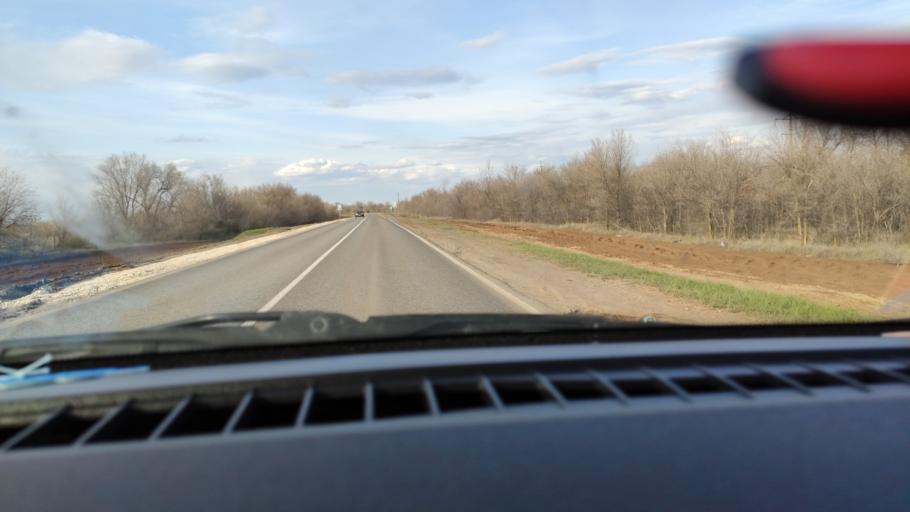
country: RU
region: Saratov
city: Privolzhskiy
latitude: 51.3265
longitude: 46.0322
